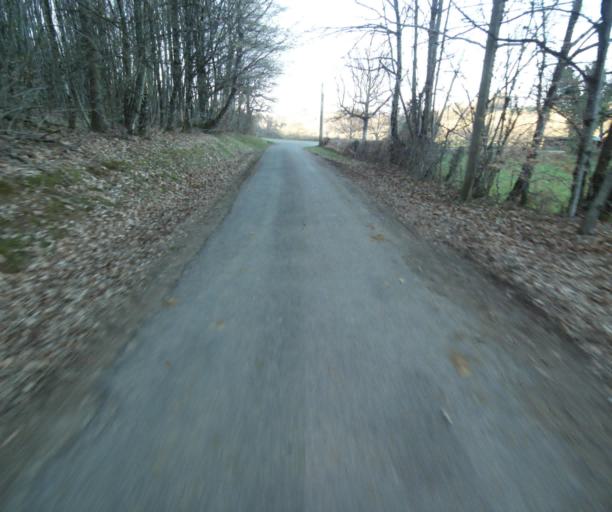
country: FR
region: Limousin
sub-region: Departement de la Correze
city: Seilhac
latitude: 45.3531
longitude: 1.7194
